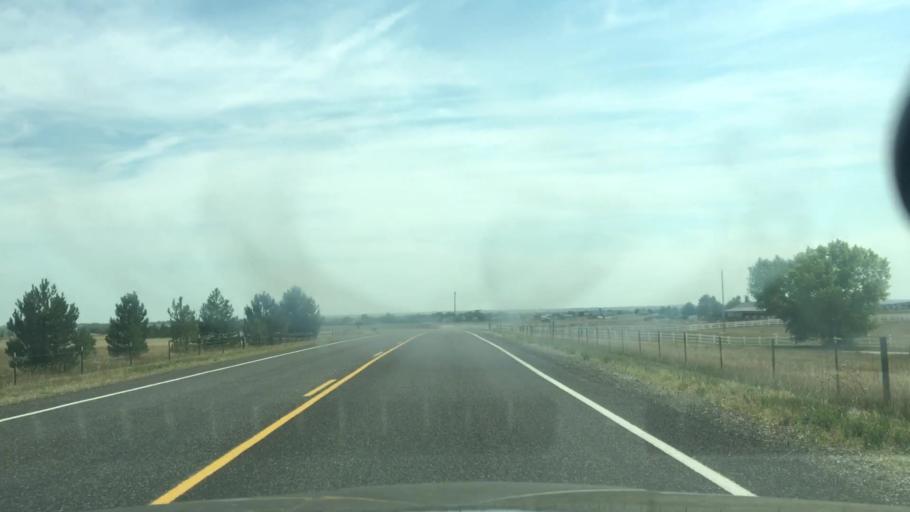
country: US
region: Colorado
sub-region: Larimer County
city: Berthoud
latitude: 40.3350
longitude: -105.1672
